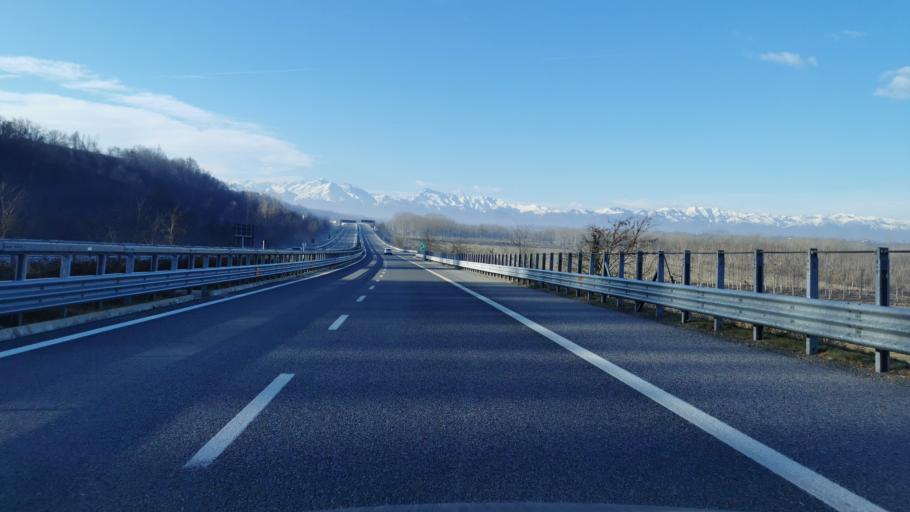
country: IT
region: Piedmont
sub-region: Provincia di Cuneo
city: Montanera
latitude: 44.4745
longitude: 7.6773
